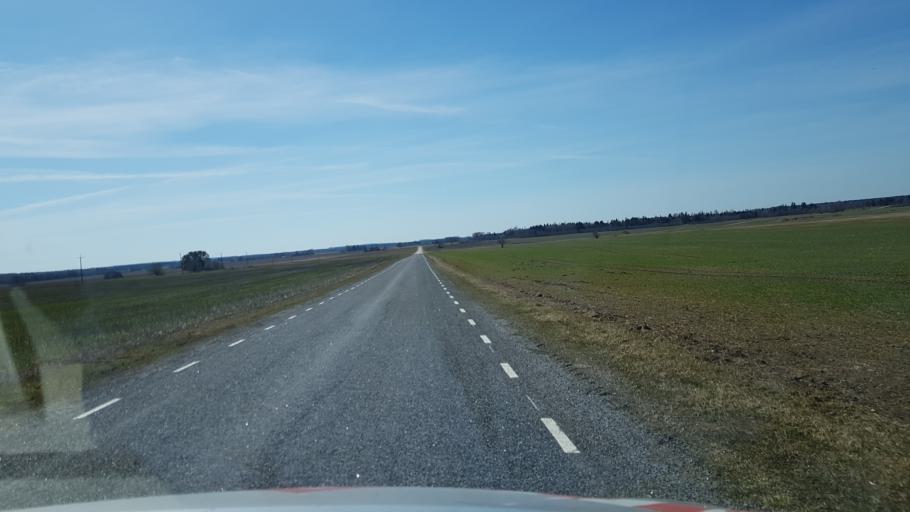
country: EE
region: Laeaene-Virumaa
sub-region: Vinni vald
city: Vinni
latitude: 59.0887
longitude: 26.4685
